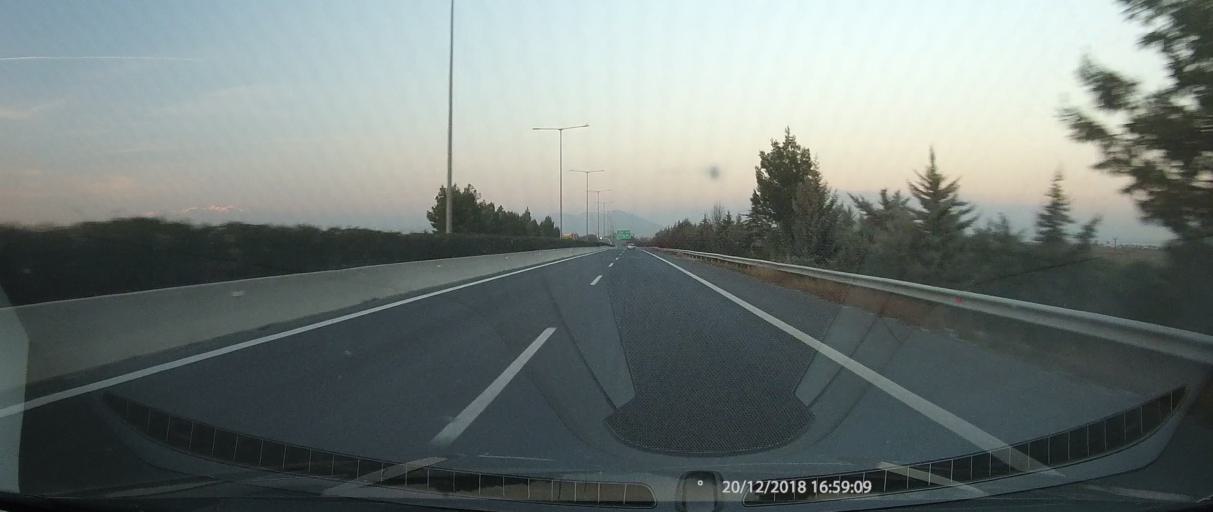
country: GR
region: Thessaly
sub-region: Nomos Larisis
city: Platykampos
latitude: 39.6083
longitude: 22.4996
